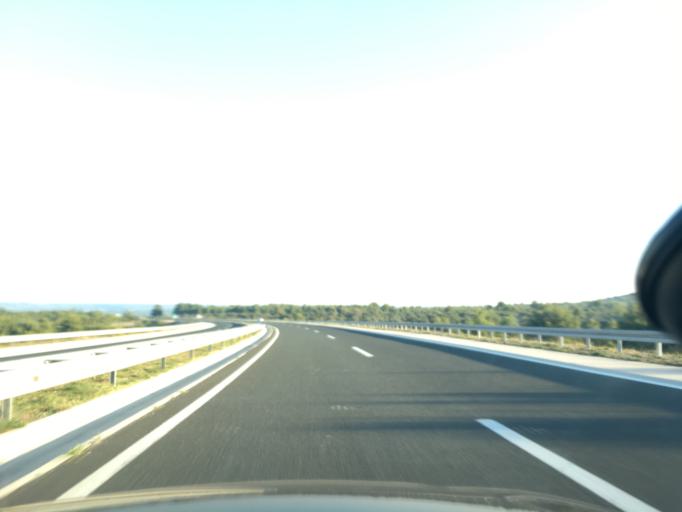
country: HR
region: Sibensko-Kniniska
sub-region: Grad Sibenik
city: Sibenik
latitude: 43.7900
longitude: 15.9193
